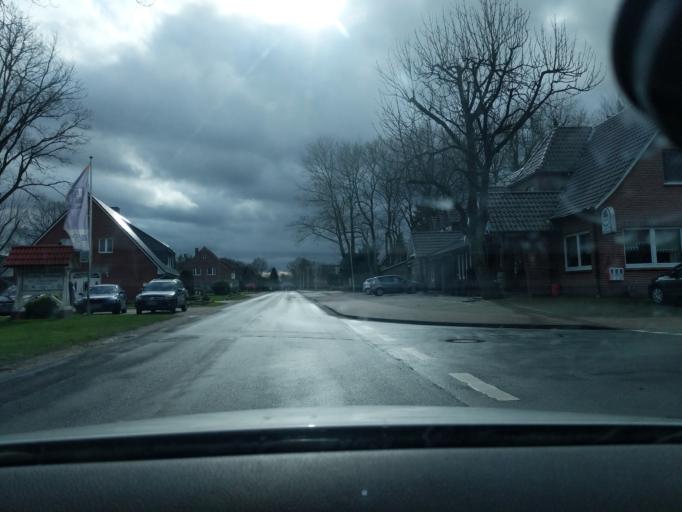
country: DE
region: Lower Saxony
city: Heinbockel
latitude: 53.5480
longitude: 9.3239
